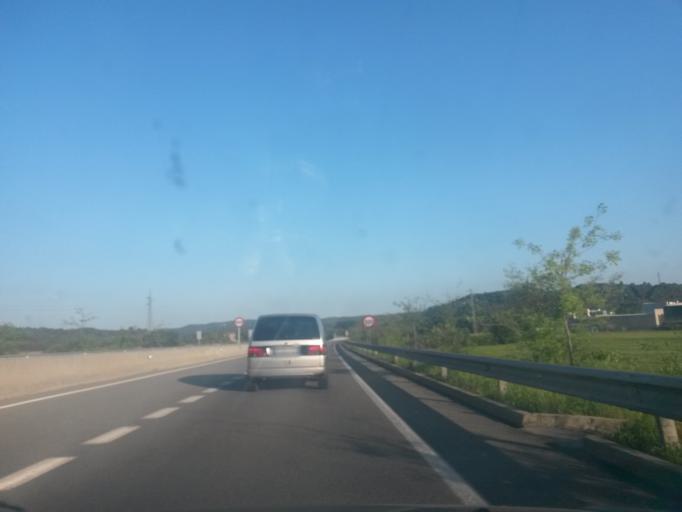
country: ES
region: Catalonia
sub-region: Provincia de Girona
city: Besalu
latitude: 42.2027
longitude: 2.7174
